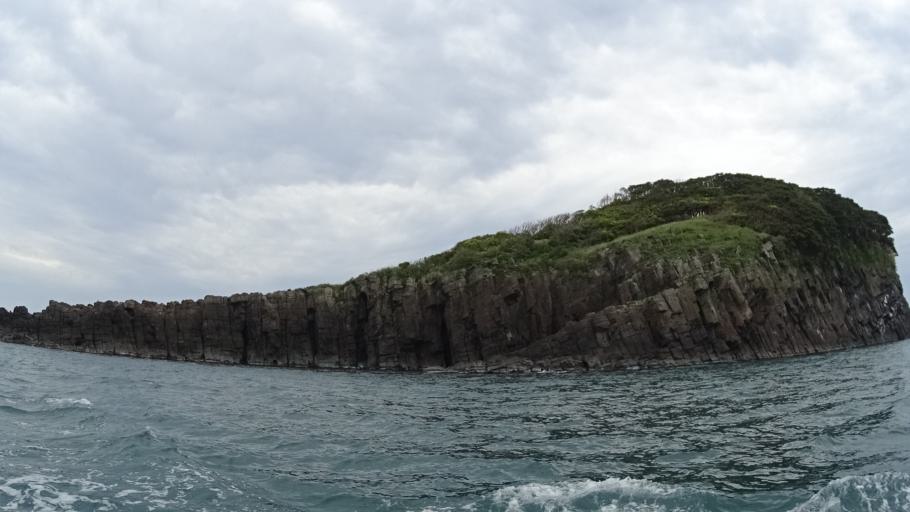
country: JP
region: Fukui
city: Mikuni
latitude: 36.2494
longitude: 136.1180
